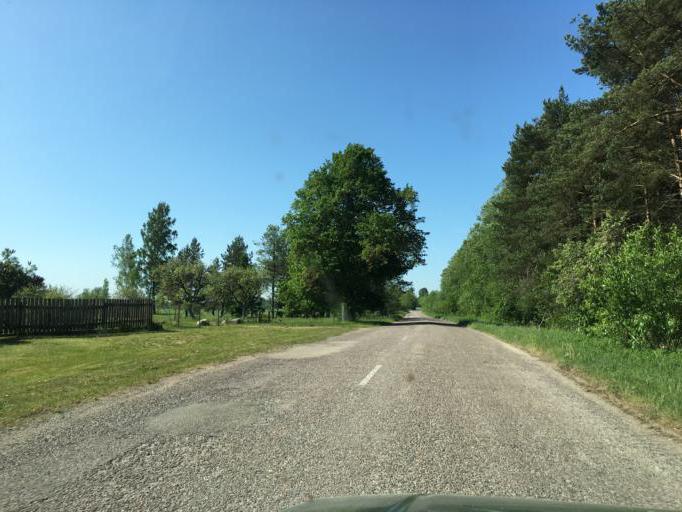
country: LV
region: Ventspils
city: Ventspils
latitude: 57.5038
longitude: 21.8470
